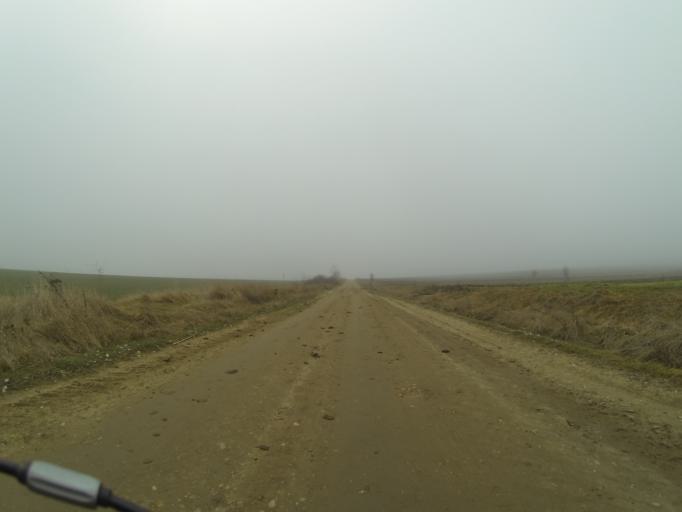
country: RO
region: Mehedinti
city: Dumbrava de Sus
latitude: 44.4817
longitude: 23.0570
